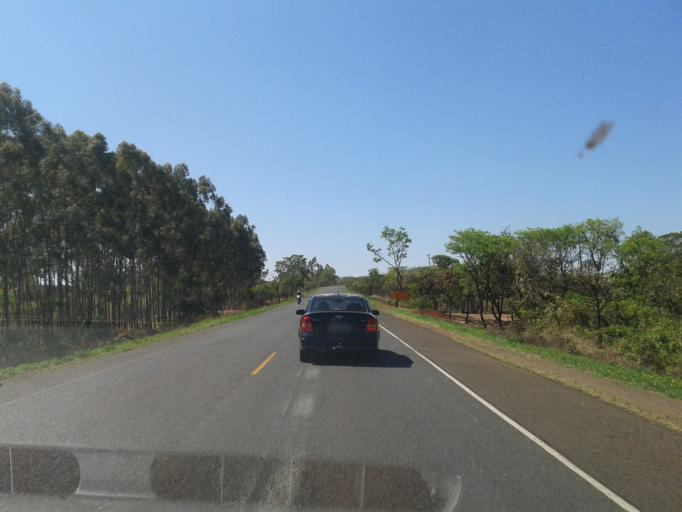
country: BR
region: Minas Gerais
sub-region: Uberlandia
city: Uberlandia
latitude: -19.0510
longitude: -48.0446
